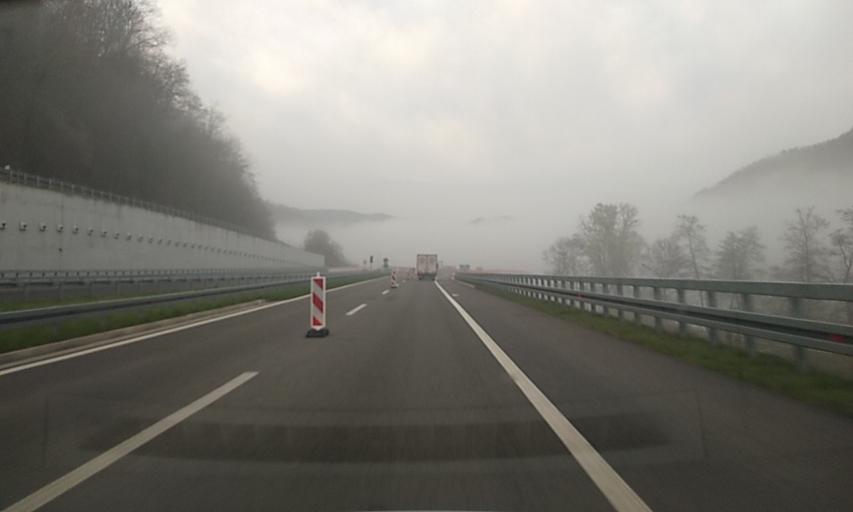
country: RS
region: Central Serbia
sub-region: Pcinjski Okrug
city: Vladicin Han
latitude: 42.7877
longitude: 22.0915
